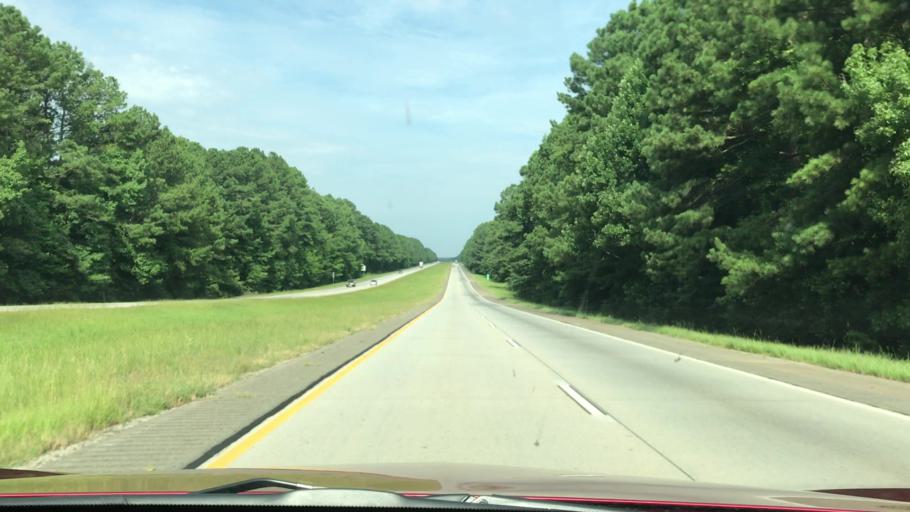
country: US
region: Georgia
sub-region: Warren County
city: Firing Range
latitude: 33.5037
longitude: -82.7297
